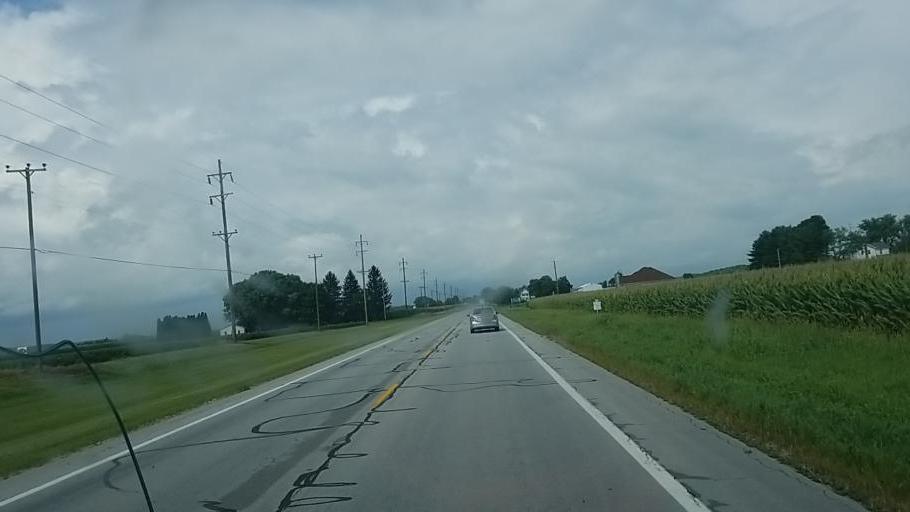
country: US
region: Ohio
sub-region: Logan County
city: West Liberty
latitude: 40.1921
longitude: -83.7418
